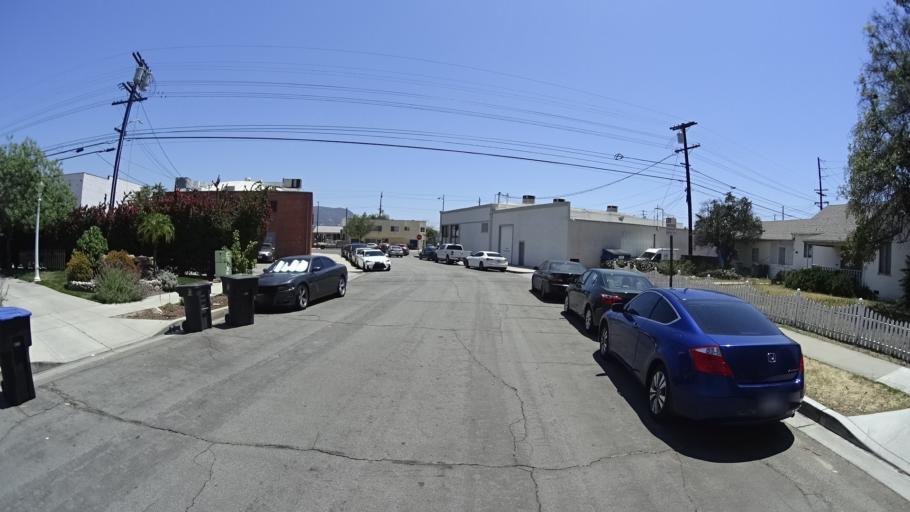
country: US
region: California
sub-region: Los Angeles County
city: North Hollywood
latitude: 34.1762
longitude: -118.3483
